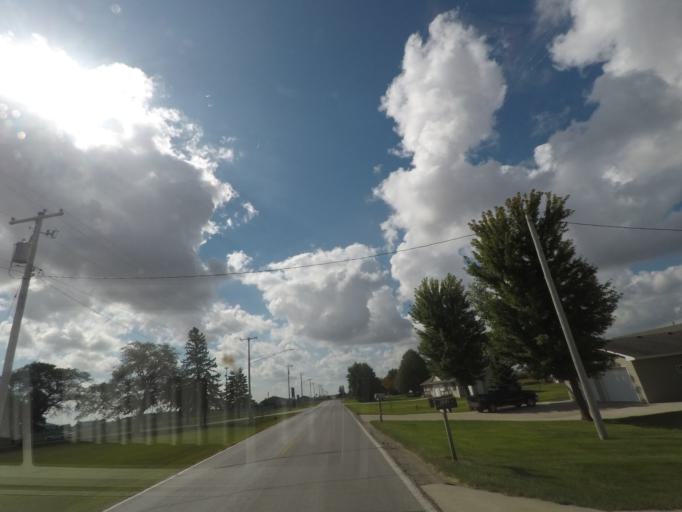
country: US
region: Iowa
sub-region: Story County
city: Nevada
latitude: 42.0105
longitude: -93.3192
